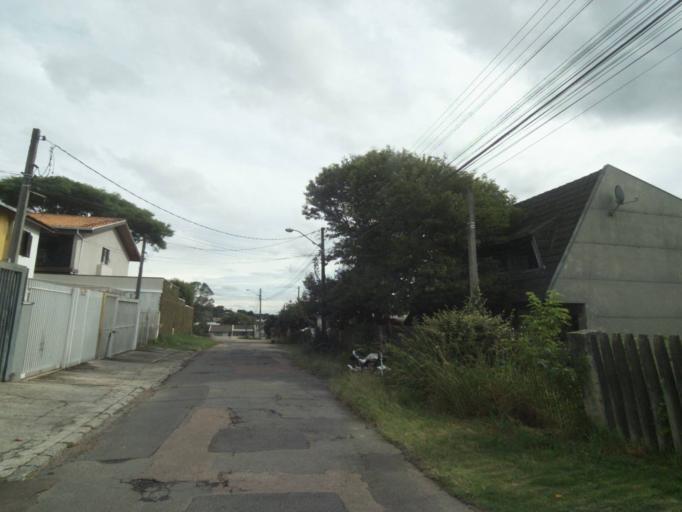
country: BR
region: Parana
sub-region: Curitiba
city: Curitiba
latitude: -25.4412
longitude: -49.3127
